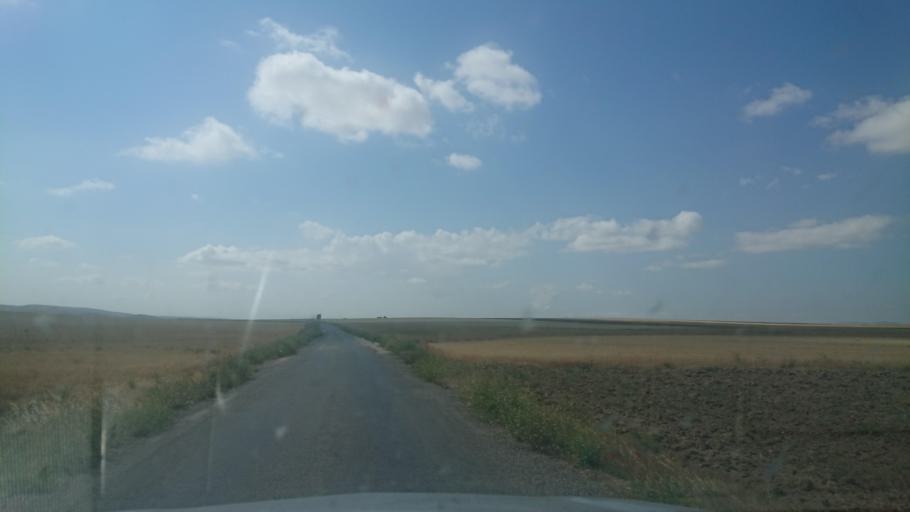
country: TR
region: Aksaray
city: Agacoren
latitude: 38.9957
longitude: 33.9814
